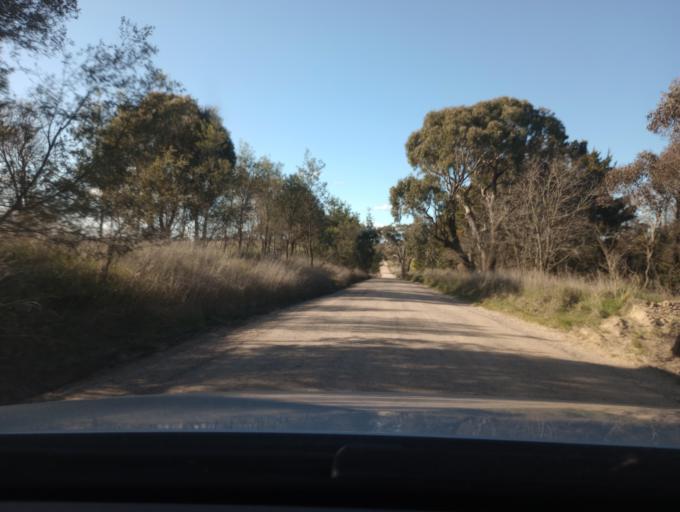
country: AU
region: New South Wales
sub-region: Blayney
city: Millthorpe
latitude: -33.4008
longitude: 149.3084
